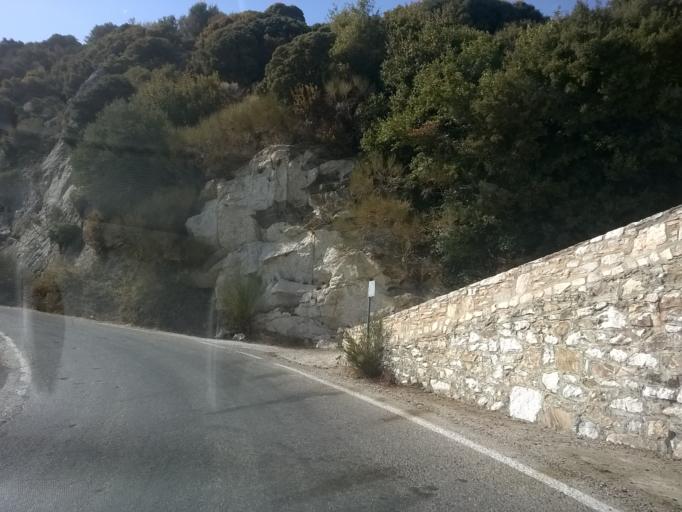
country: GR
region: South Aegean
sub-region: Nomos Kykladon
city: Filotion
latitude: 37.1256
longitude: 25.5336
